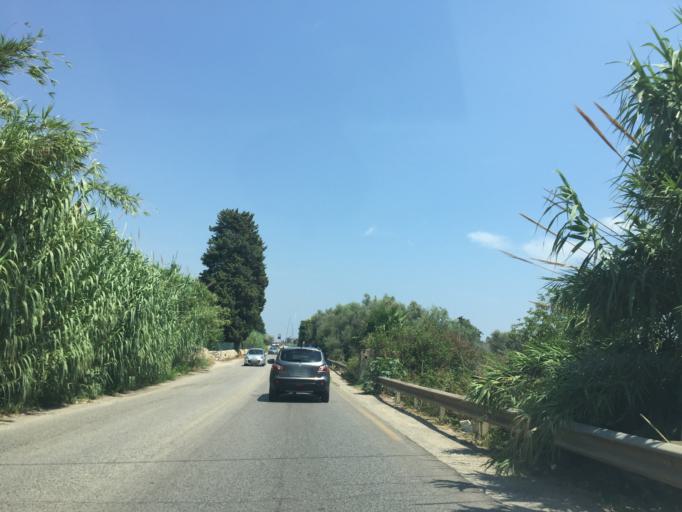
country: IT
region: Sicily
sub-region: Provincia di Siracusa
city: Avola
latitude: 36.9222
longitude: 15.1534
